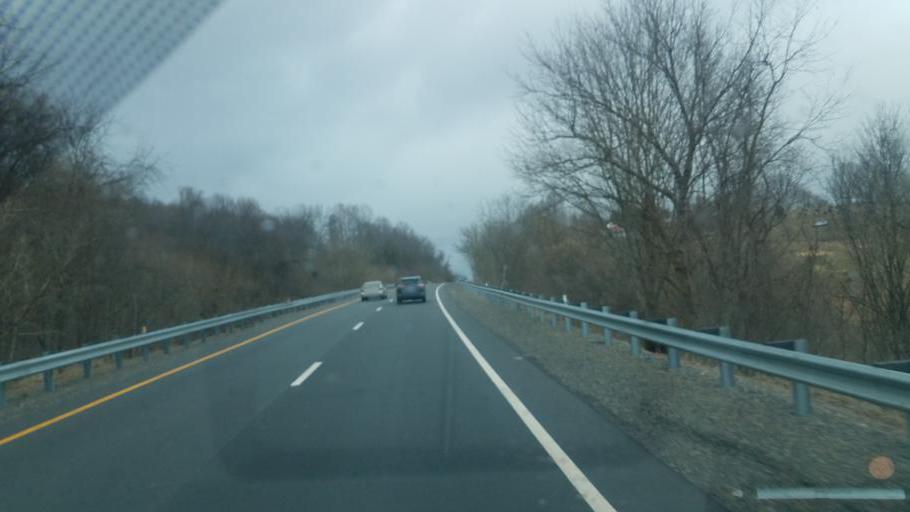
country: US
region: Virginia
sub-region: Giles County
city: Pearisburg
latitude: 37.2948
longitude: -80.7410
